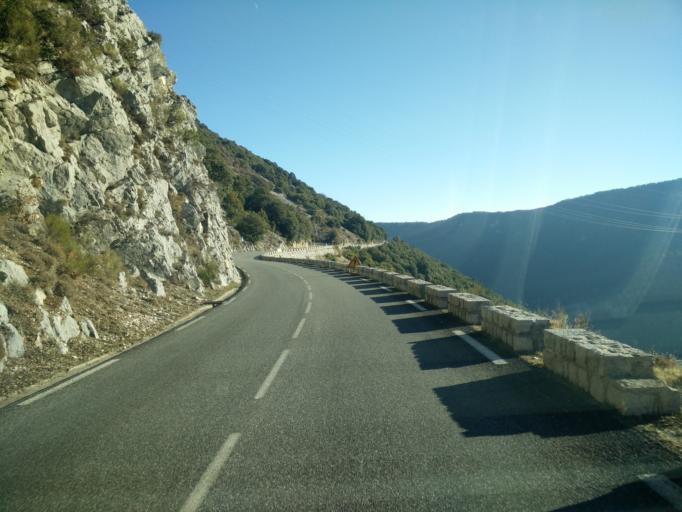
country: FR
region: Provence-Alpes-Cote d'Azur
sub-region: Departement des Alpes-Maritimes
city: Saint-Vallier-de-Thiey
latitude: 43.7277
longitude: 6.8159
